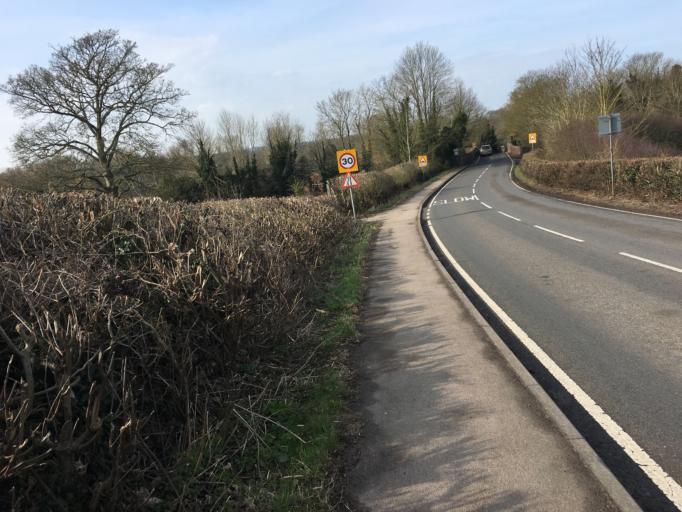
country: GB
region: England
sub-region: Warwickshire
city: Rugby
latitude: 52.3913
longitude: -1.2751
